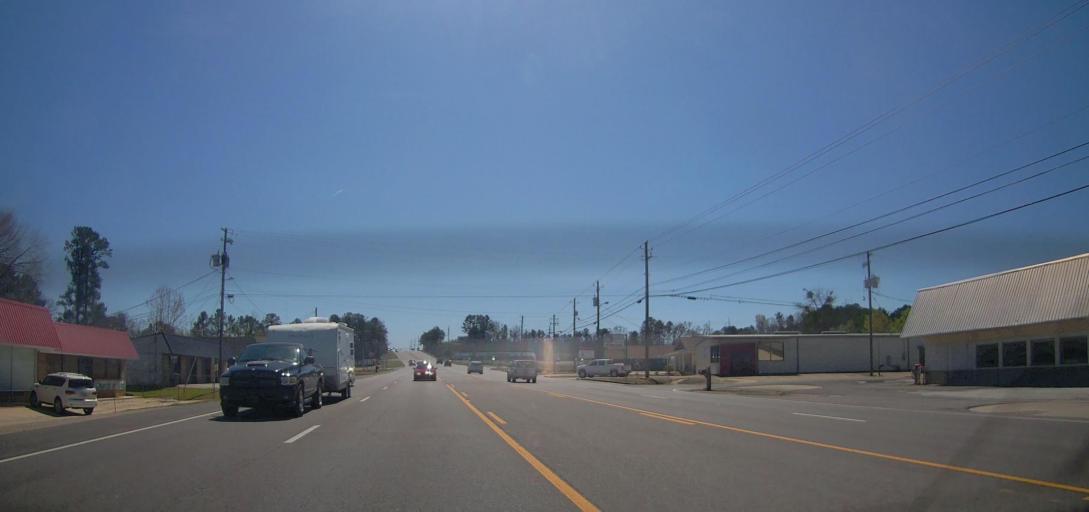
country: US
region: Alabama
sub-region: Etowah County
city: Southside
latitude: 33.9309
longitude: -86.0241
